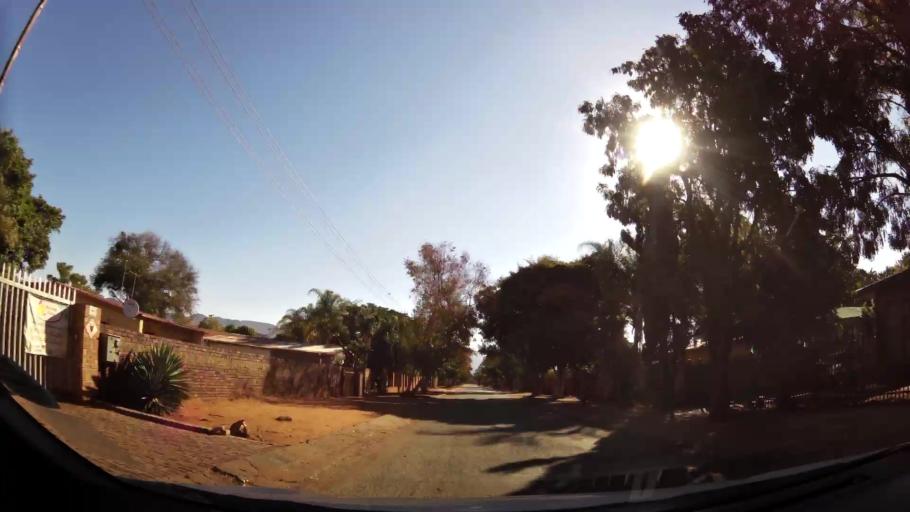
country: ZA
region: Limpopo
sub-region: Waterberg District Municipality
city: Mokopane
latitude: -24.1778
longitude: 28.9972
